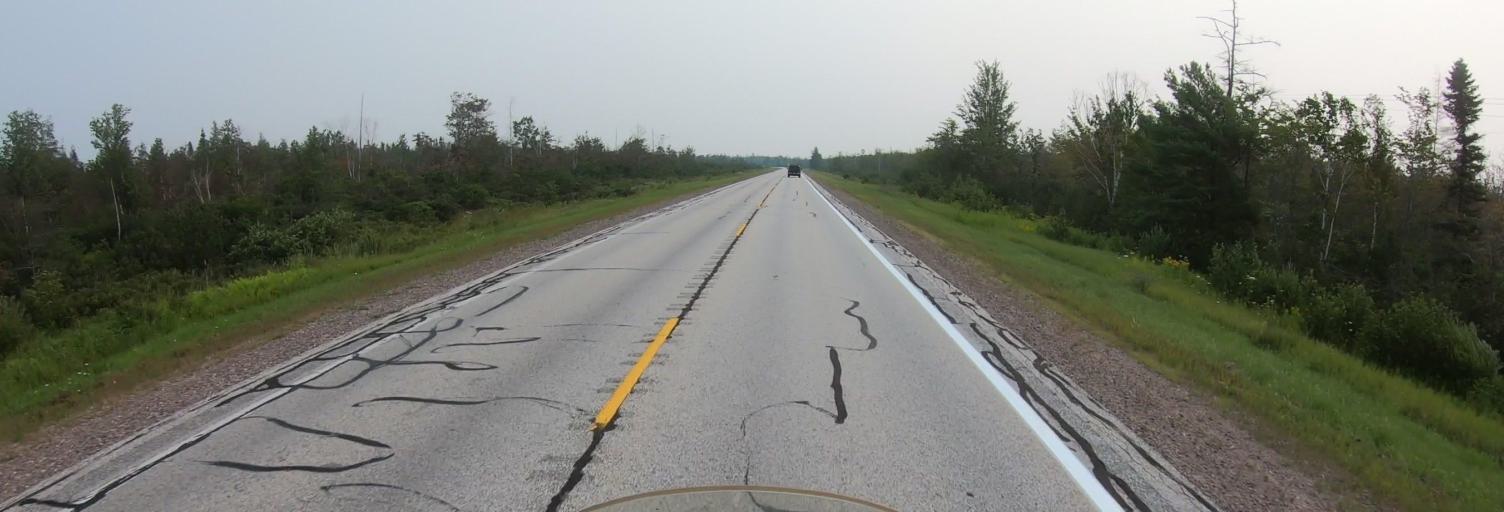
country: US
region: Michigan
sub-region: Luce County
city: Newberry
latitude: 46.5350
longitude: -85.0561
